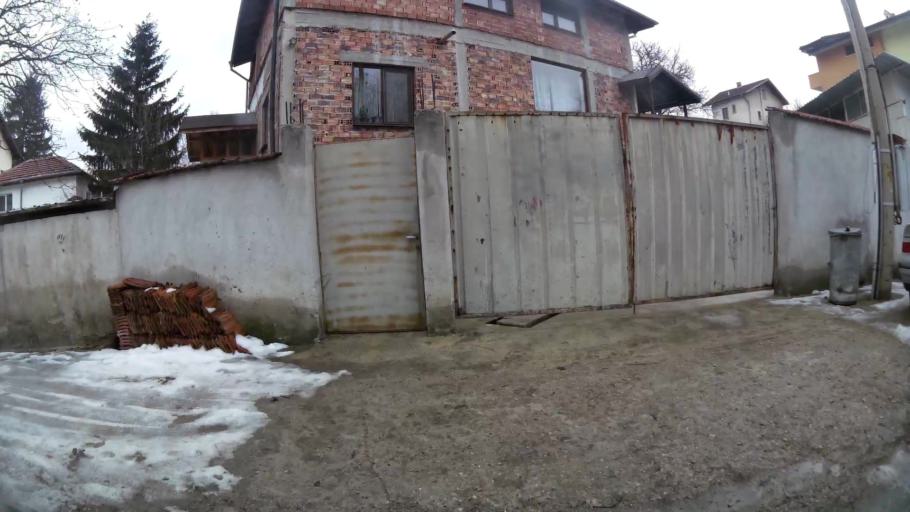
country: BG
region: Sofiya
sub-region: Obshtina Bozhurishte
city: Bozhurishte
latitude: 42.6967
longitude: 23.2198
